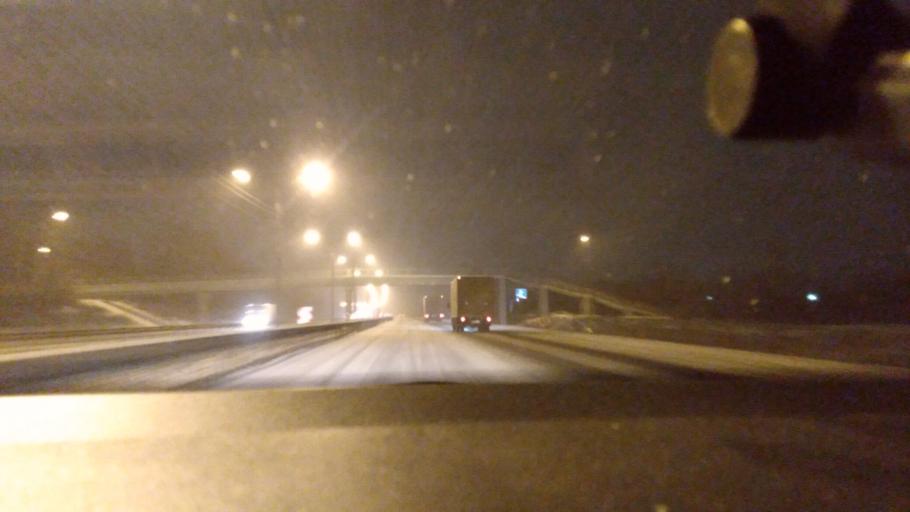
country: RU
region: Moskovskaya
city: Zhukovskiy
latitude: 55.5292
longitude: 38.1094
